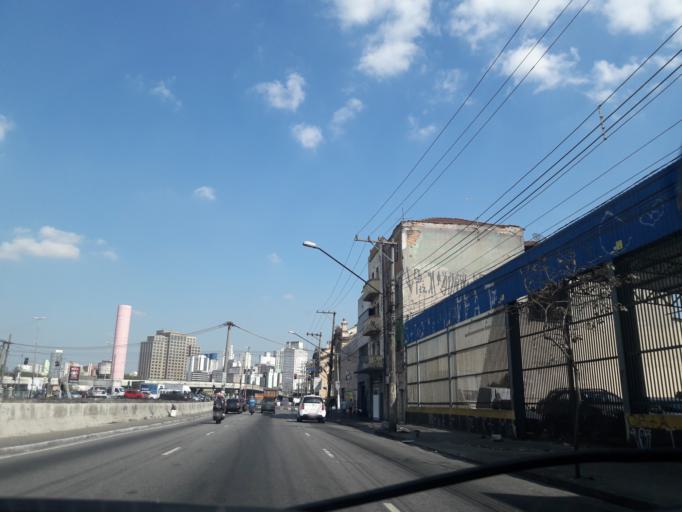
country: BR
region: Sao Paulo
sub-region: Sao Paulo
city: Sao Paulo
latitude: -23.5404
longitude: -46.6281
